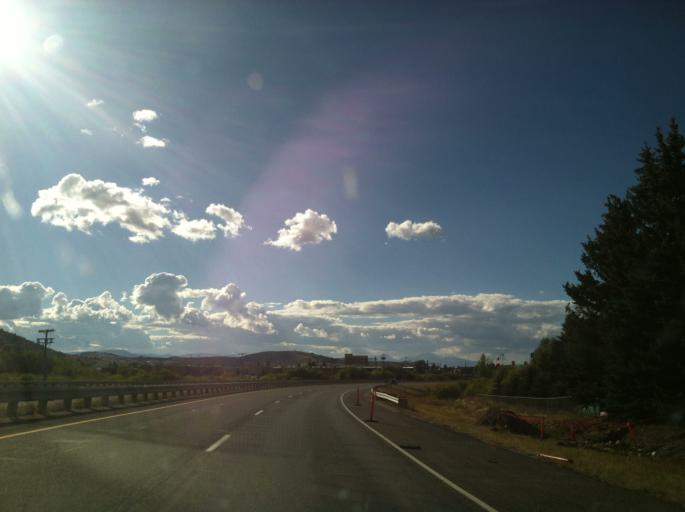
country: US
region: Montana
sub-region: Silver Bow County
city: Butte
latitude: 45.9798
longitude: -112.4998
